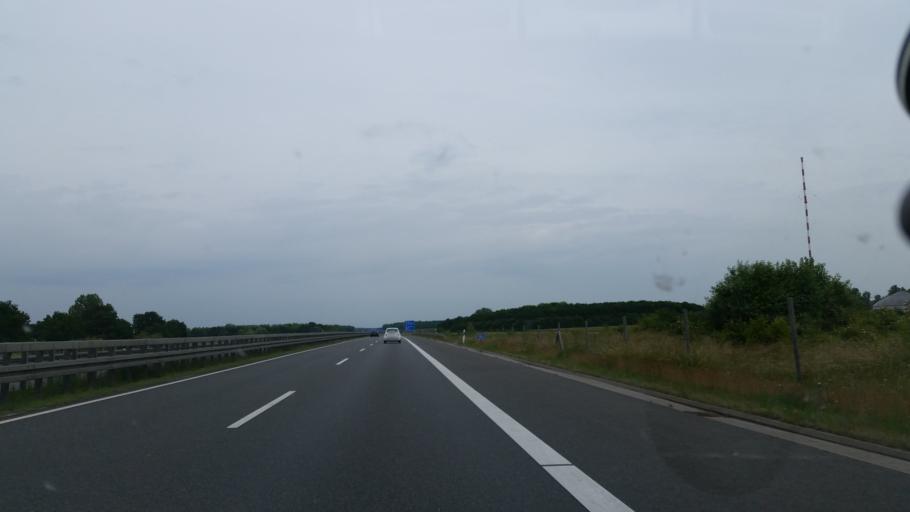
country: DE
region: Lower Saxony
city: Lehre
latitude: 52.2884
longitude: 10.7156
